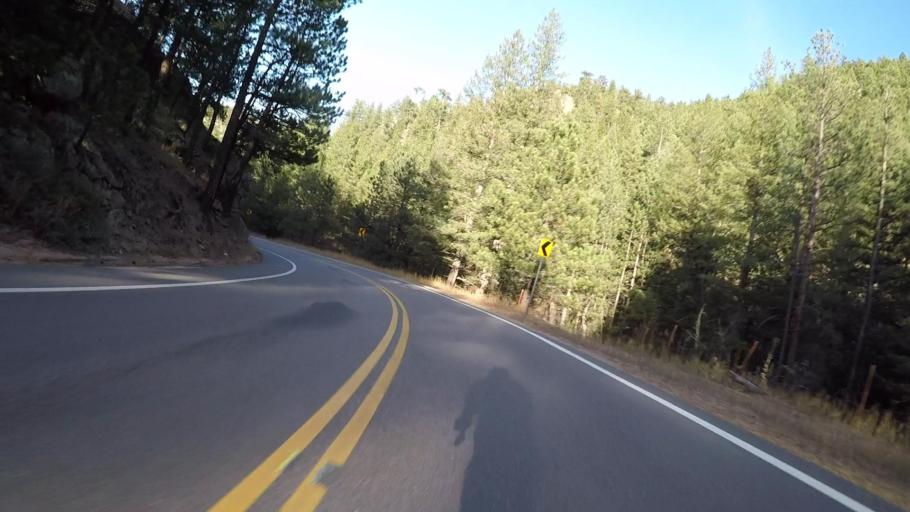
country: US
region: Colorado
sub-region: Boulder County
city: Boulder
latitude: 40.0987
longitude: -105.3441
